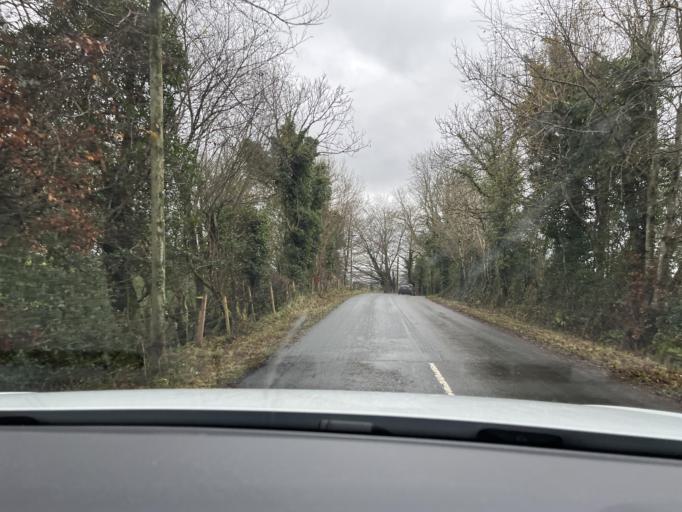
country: IE
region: Connaught
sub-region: County Leitrim
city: Manorhamilton
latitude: 54.2750
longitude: -8.2104
